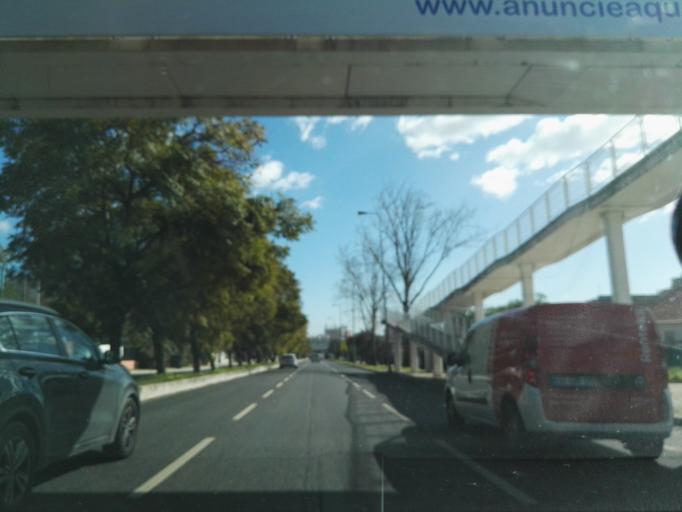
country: PT
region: Lisbon
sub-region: Loures
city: Moscavide
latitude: 38.7791
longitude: -9.1162
